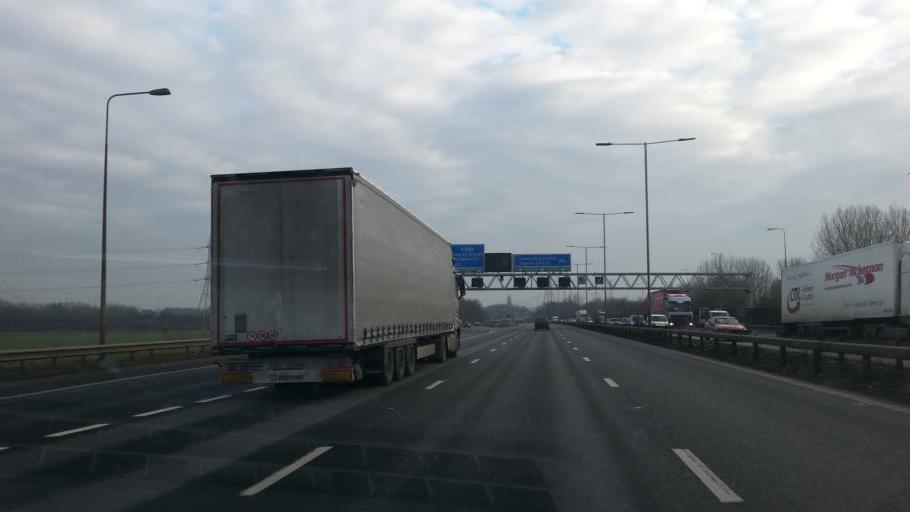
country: GB
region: England
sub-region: Solihull
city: Chelmsley Wood
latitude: 52.4845
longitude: -1.7246
